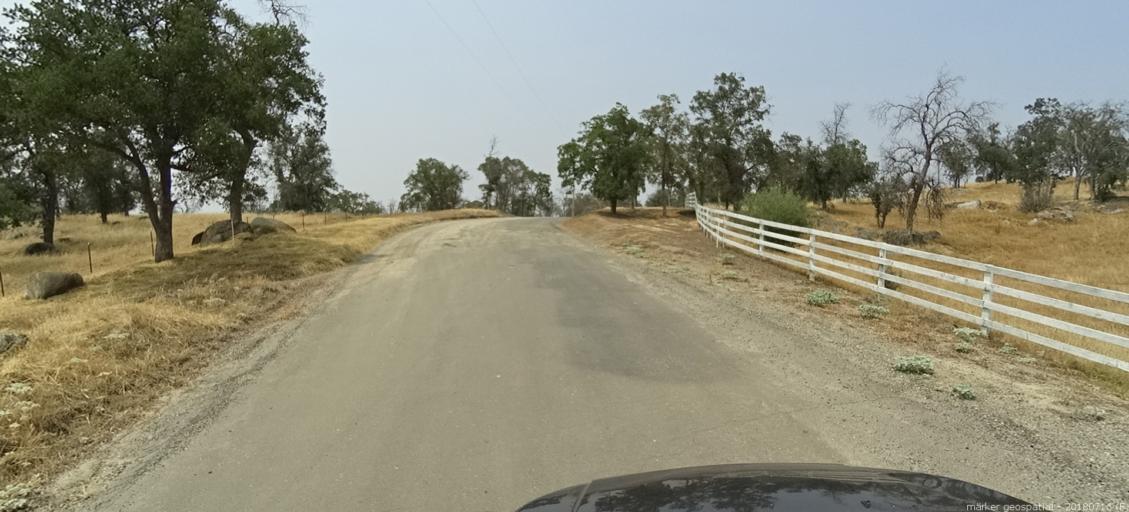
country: US
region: California
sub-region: Madera County
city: Yosemite Lakes
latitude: 37.2329
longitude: -119.7920
